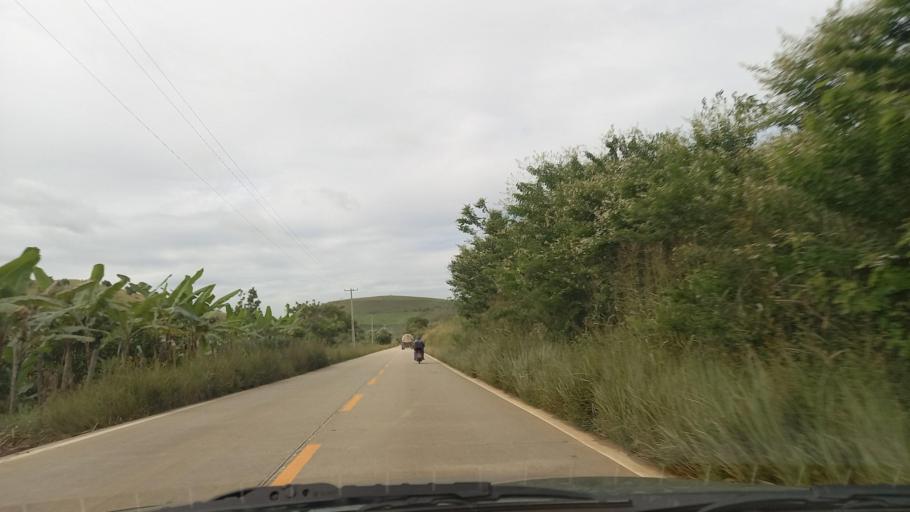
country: BR
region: Pernambuco
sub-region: Maraial
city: Maraial
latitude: -8.7533
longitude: -35.8395
